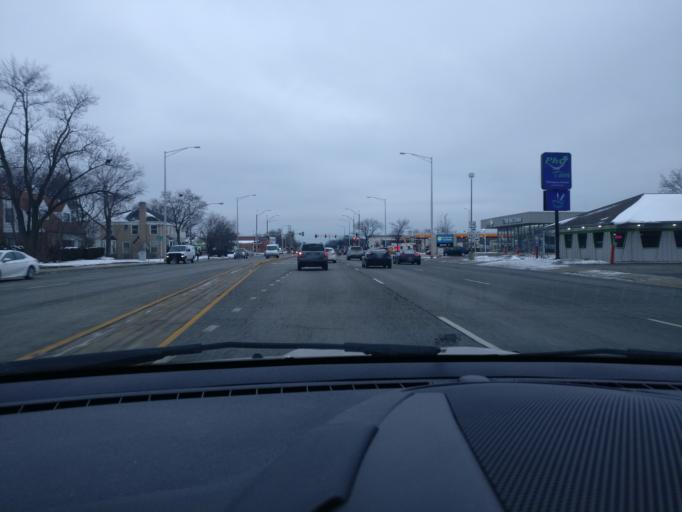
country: US
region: Illinois
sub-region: Cook County
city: Morton Grove
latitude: 42.0408
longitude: -87.8013
